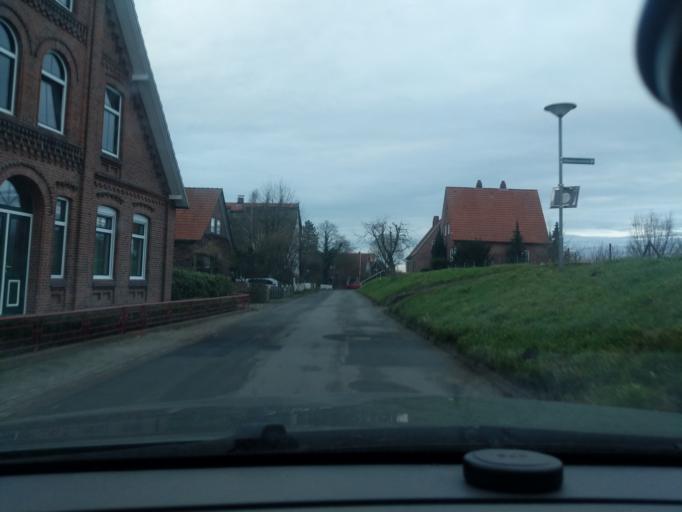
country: DE
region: Lower Saxony
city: Guderhandviertel
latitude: 53.5377
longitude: 9.6110
